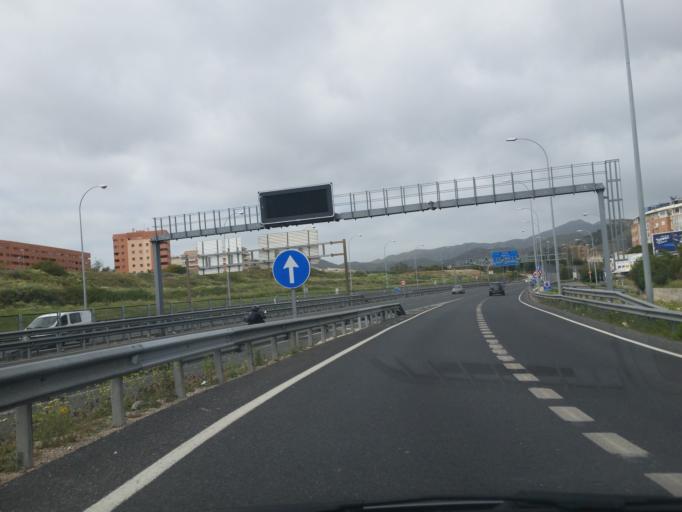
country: ES
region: Andalusia
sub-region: Provincia de Malaga
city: Malaga
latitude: 36.7152
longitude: -4.4578
